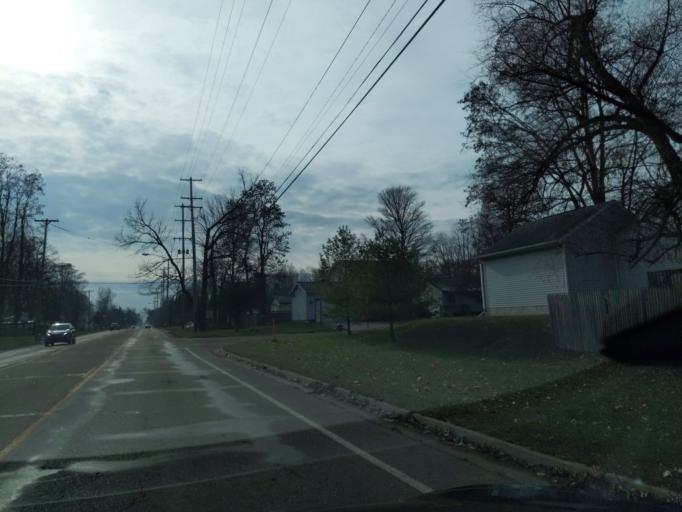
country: US
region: Michigan
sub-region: Ingham County
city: Holt
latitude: 42.6589
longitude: -84.5235
